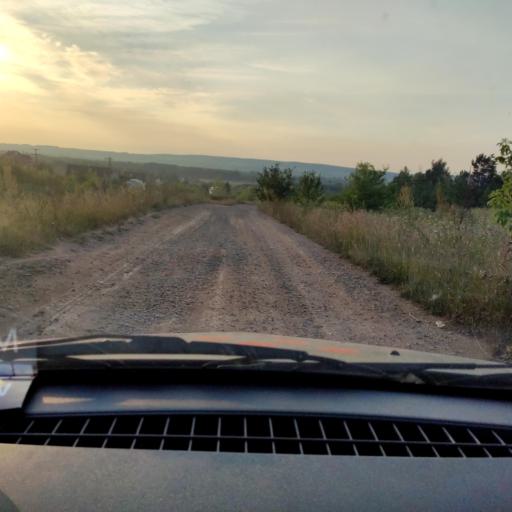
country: RU
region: Bashkortostan
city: Avdon
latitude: 54.5867
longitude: 55.6798
